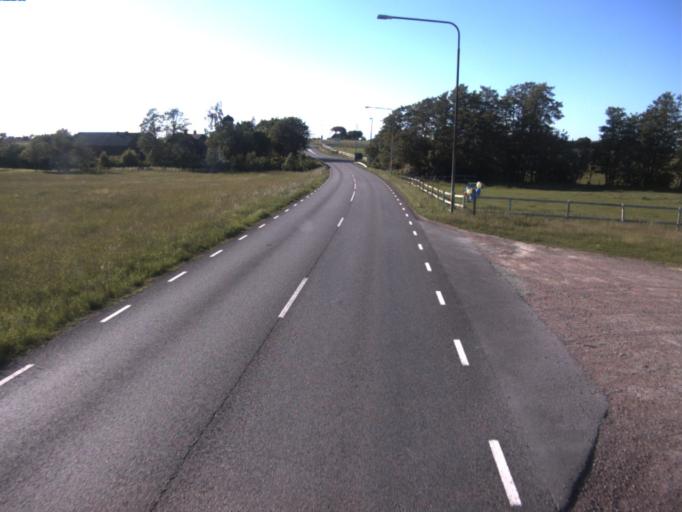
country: SE
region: Skane
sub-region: Helsingborg
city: Rydeback
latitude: 55.9751
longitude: 12.7765
